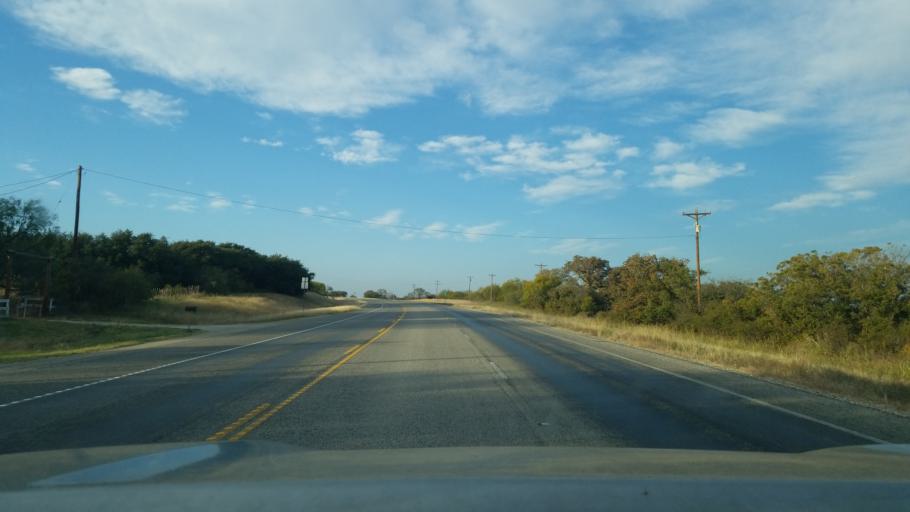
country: US
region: Texas
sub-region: Brown County
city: Lake Brownwood
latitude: 32.0065
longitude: -98.9211
